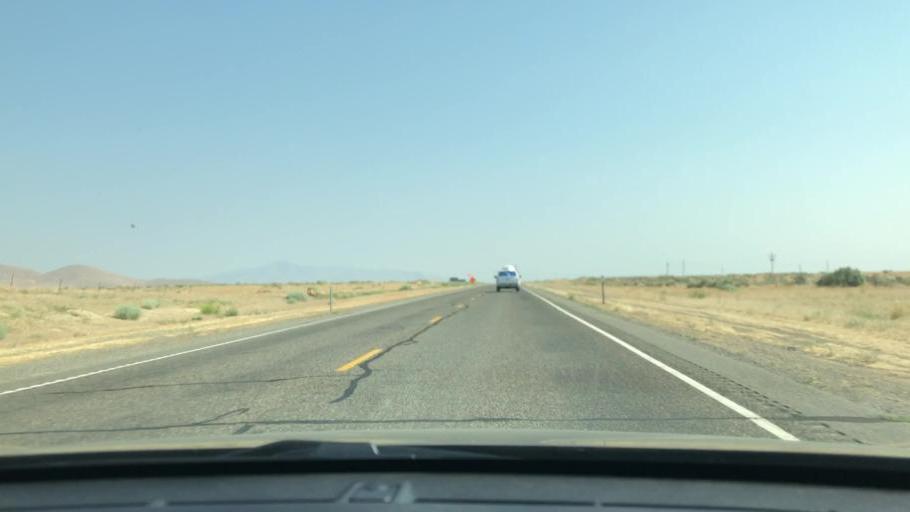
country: US
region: Nevada
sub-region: Humboldt County
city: Winnemucca
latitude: 41.1452
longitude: -117.6887
